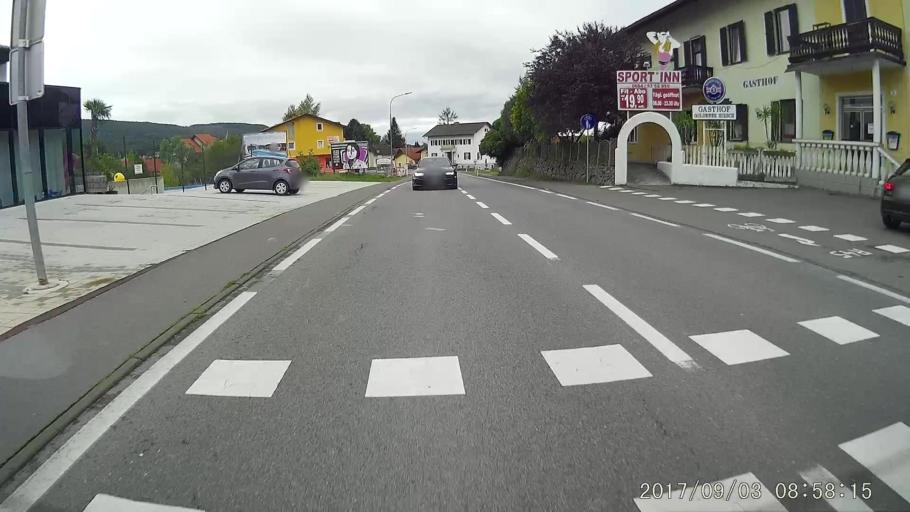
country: AT
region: Styria
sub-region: Politischer Bezirk Suedoststeiermark
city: Merkendorf
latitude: 46.8668
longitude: 15.9026
